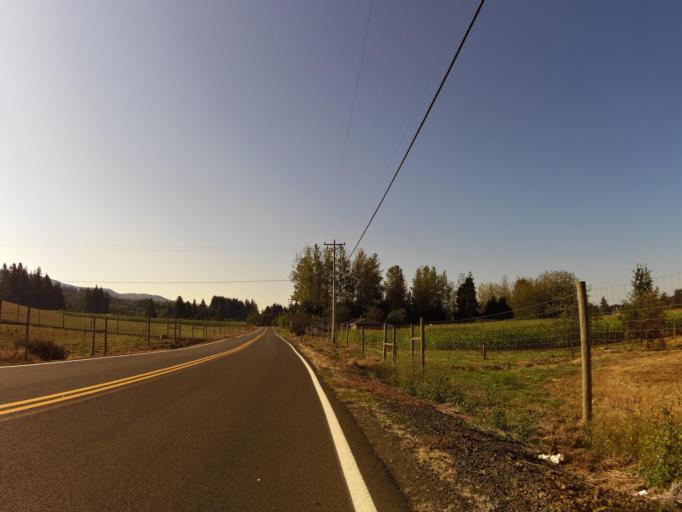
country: US
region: Oregon
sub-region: Tillamook County
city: Tillamook
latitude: 45.3914
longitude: -123.7943
